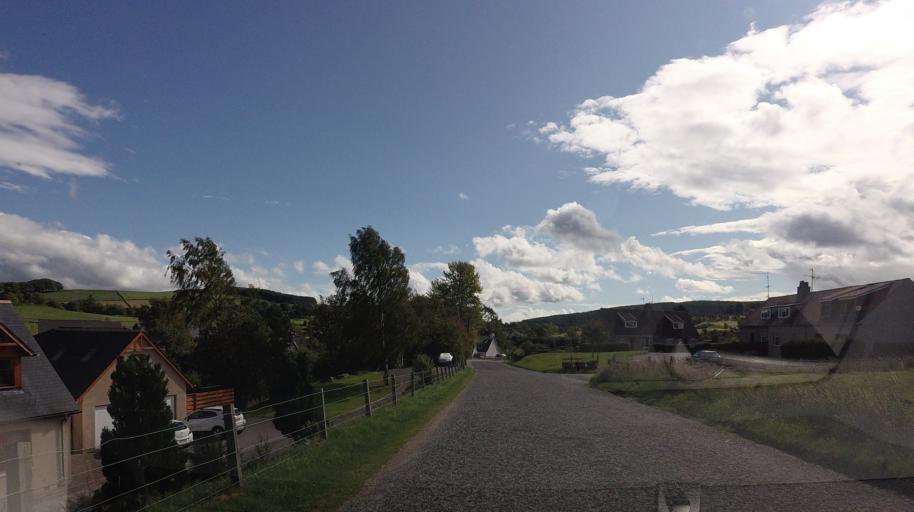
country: GB
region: Scotland
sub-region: Aberdeenshire
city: Torphins
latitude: 57.1312
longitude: -2.6918
